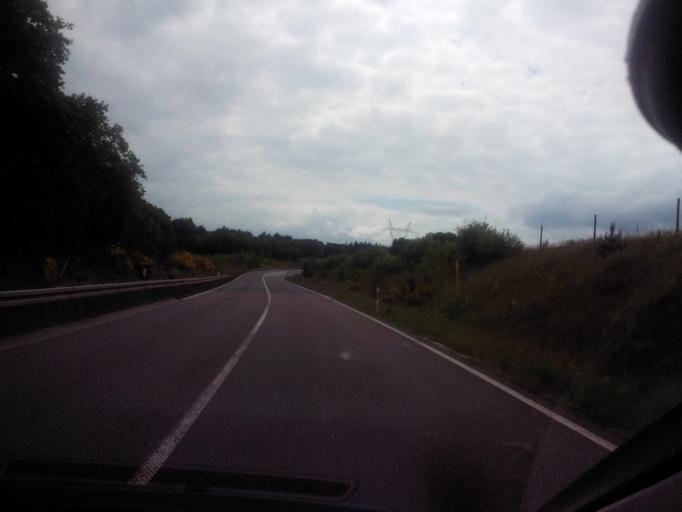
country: DE
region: Saarland
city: Uberherrn
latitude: 49.2362
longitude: 6.7148
